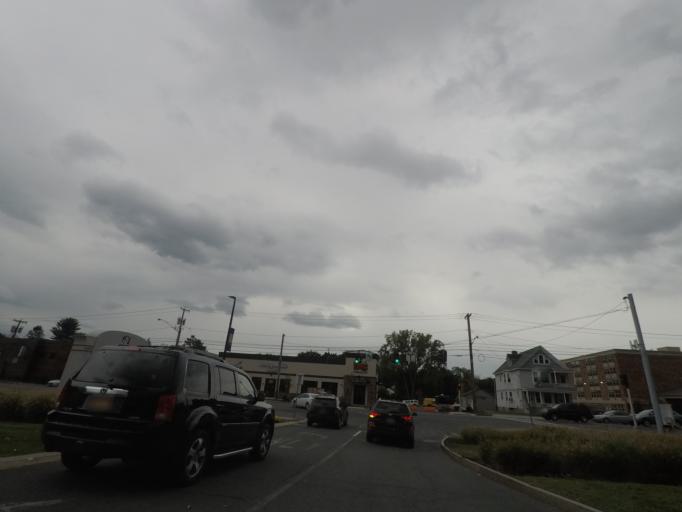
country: US
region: New York
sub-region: Albany County
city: McKownville
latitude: 42.6781
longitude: -73.8269
